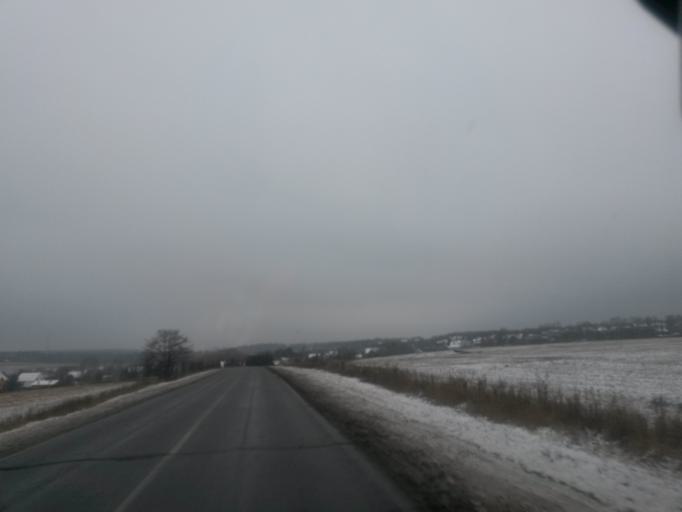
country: RU
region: Moskovskaya
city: Lyubuchany
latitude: 55.2622
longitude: 37.6080
